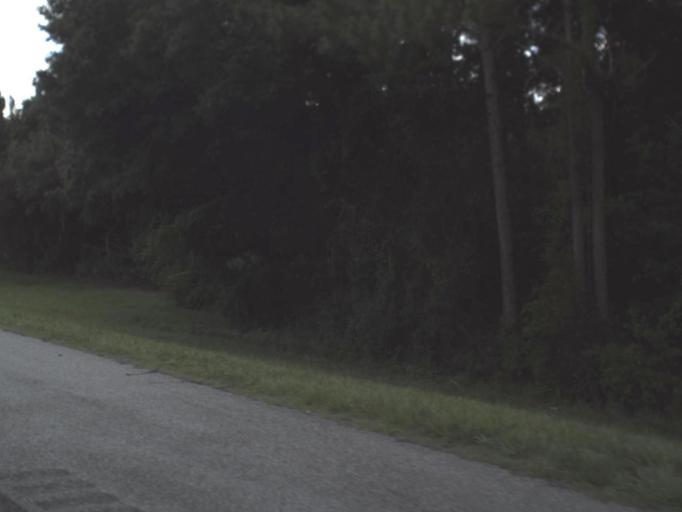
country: US
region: Florida
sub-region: Suwannee County
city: Wellborn
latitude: 30.3388
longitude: -82.8270
